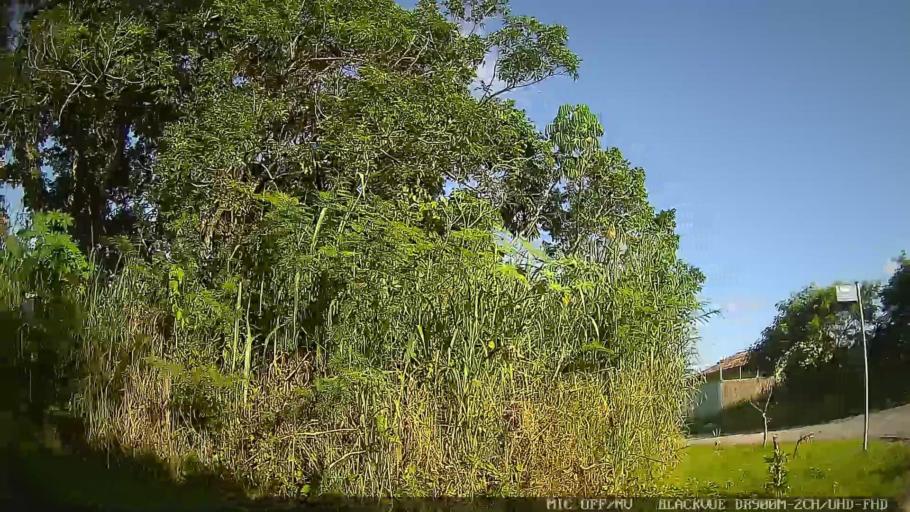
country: BR
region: Sao Paulo
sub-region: Peruibe
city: Peruibe
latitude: -24.2831
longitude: -46.9625
